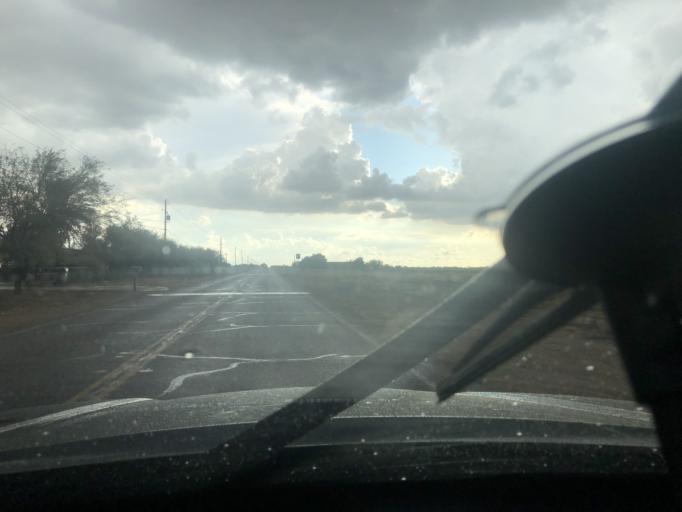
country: US
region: Arizona
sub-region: Maricopa County
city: Scottsdale
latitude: 33.4871
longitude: -111.8828
